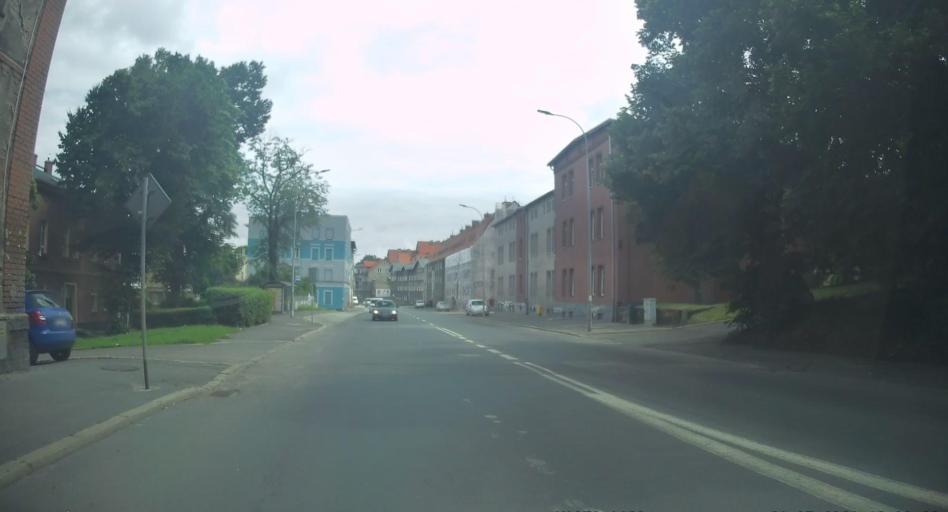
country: PL
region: Lower Silesian Voivodeship
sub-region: Powiat walbrzyski
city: Walbrzych
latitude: 50.7649
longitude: 16.2561
